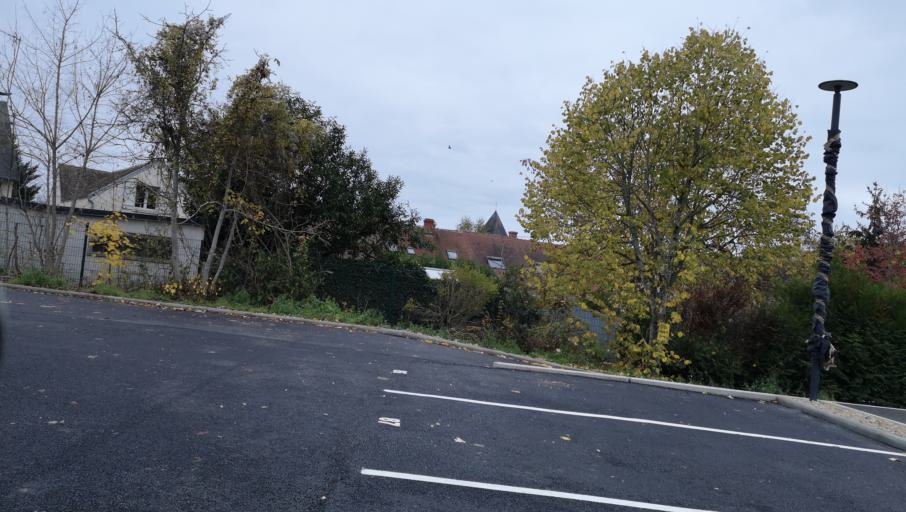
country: FR
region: Centre
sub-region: Departement du Loiret
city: Saint-Jean-de-Braye
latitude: 47.9052
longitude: 1.9663
